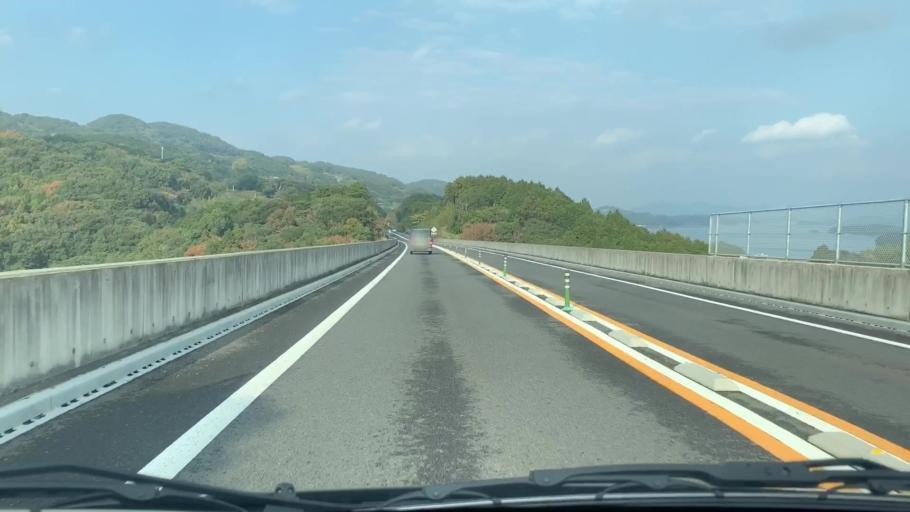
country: JP
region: Nagasaki
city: Sasebo
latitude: 33.0110
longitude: 129.7295
